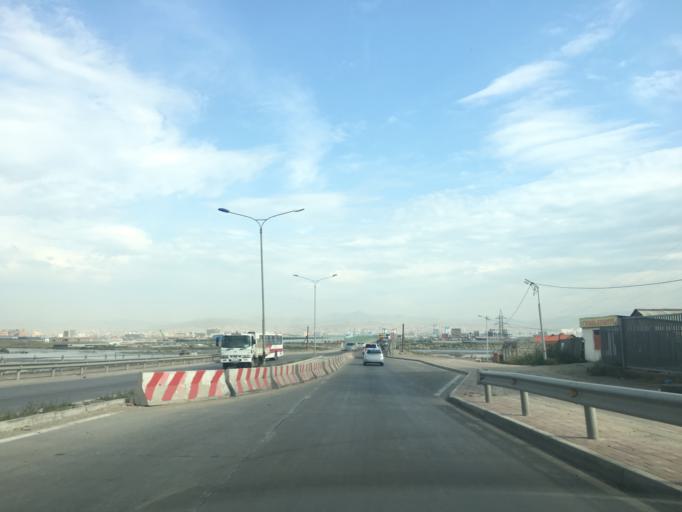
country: MN
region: Ulaanbaatar
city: Ulaanbaatar
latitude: 47.8718
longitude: 106.7844
